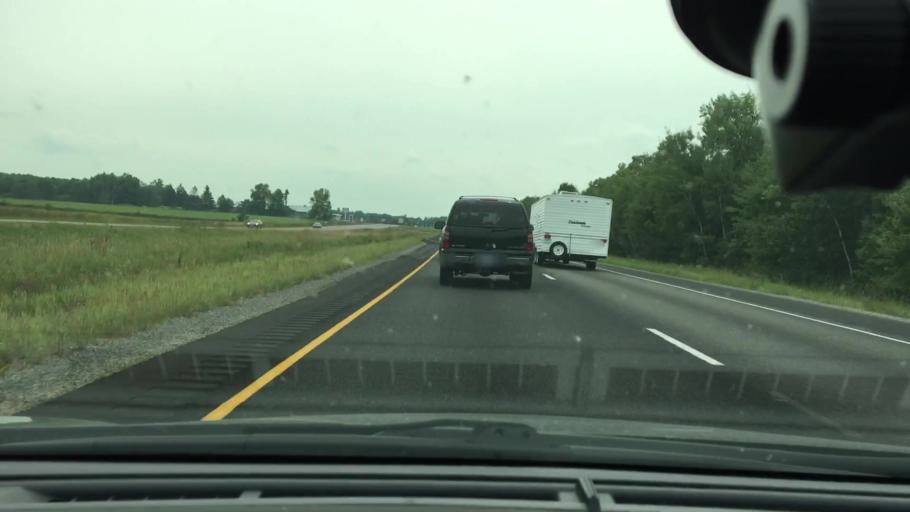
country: US
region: Minnesota
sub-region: Mille Lacs County
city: Milaca
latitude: 45.8289
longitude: -93.6603
